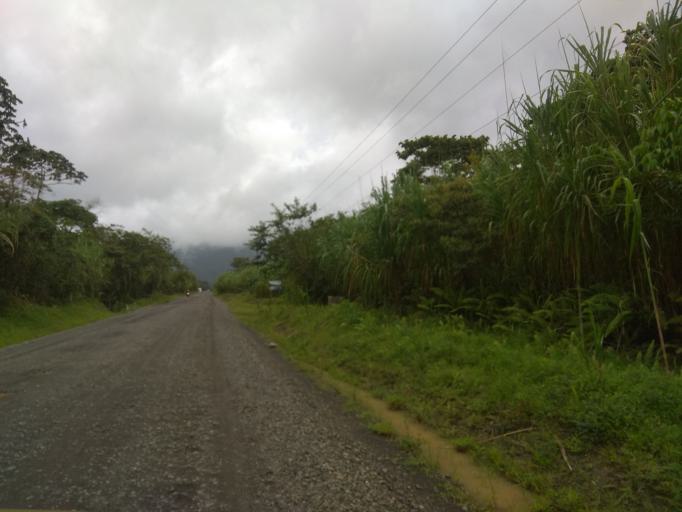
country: CR
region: Alajuela
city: La Fortuna
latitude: 10.4597
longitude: -84.7397
